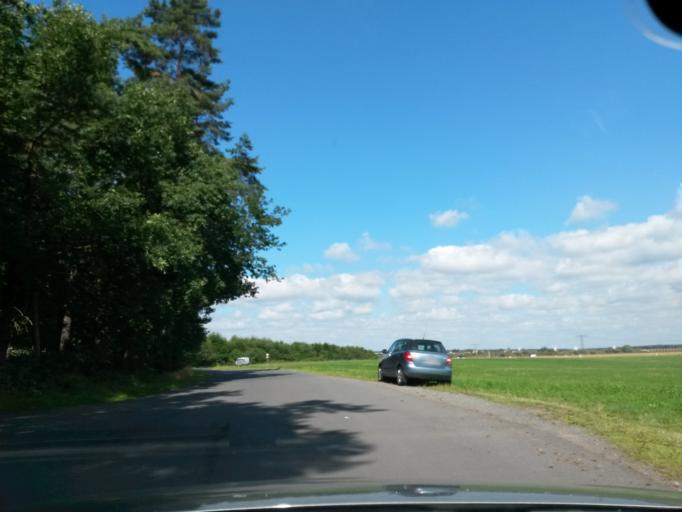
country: DE
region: Thuringia
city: Reichenbach
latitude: 50.8782
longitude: 11.8699
